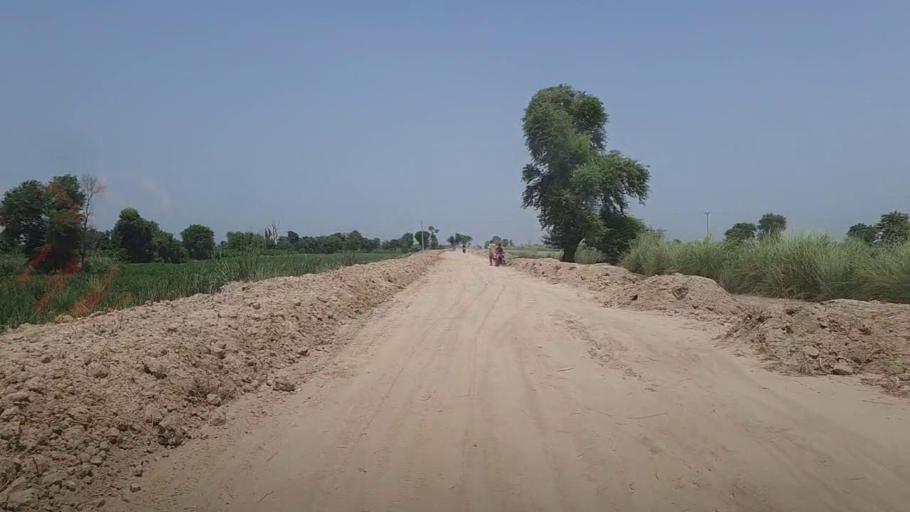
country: PK
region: Sindh
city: Pad Idan
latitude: 26.7941
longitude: 68.2751
